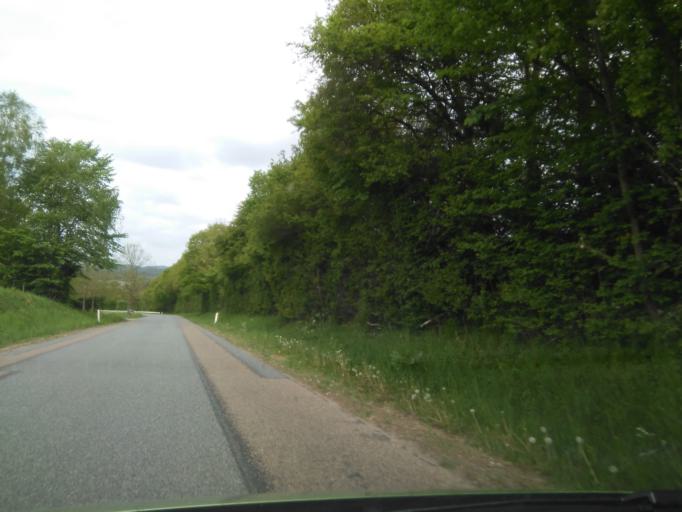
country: DK
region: Central Jutland
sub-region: Skanderborg Kommune
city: Ry
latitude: 56.0546
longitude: 9.7756
